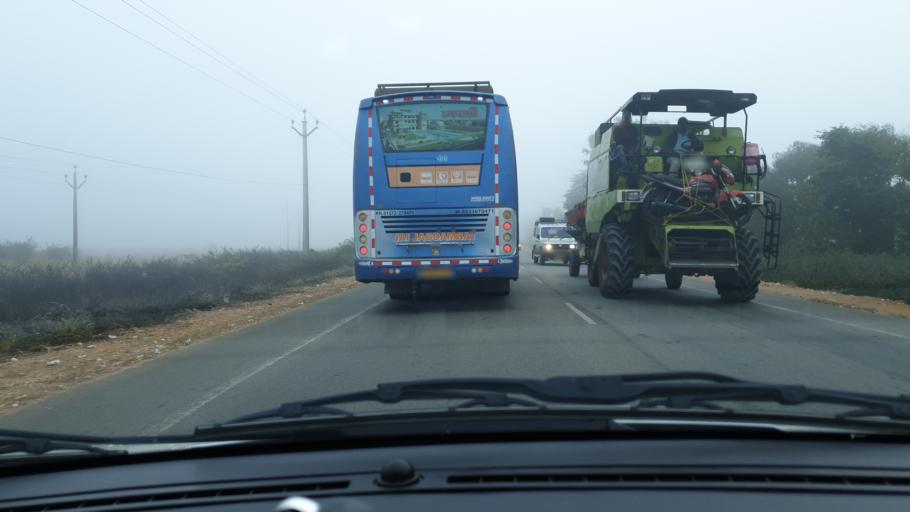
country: IN
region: Telangana
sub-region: Mahbubnagar
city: Nagar Karnul
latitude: 16.6645
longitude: 78.5497
